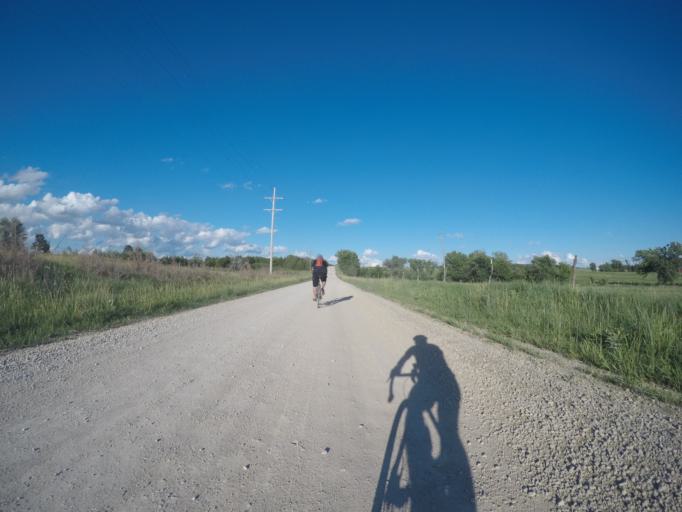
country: US
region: Kansas
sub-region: Riley County
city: Manhattan
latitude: 39.2616
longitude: -96.6883
